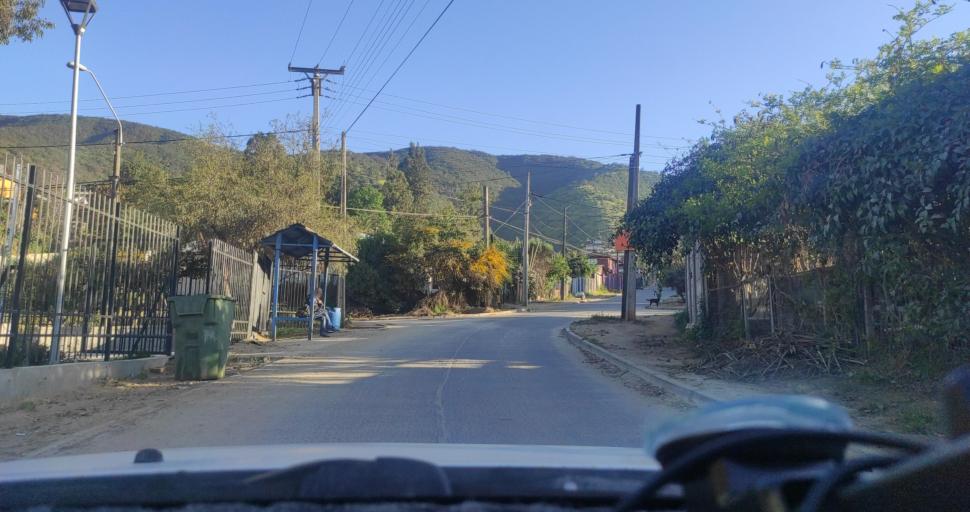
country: CL
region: Valparaiso
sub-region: Provincia de Marga Marga
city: Limache
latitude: -32.9885
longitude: -71.2359
